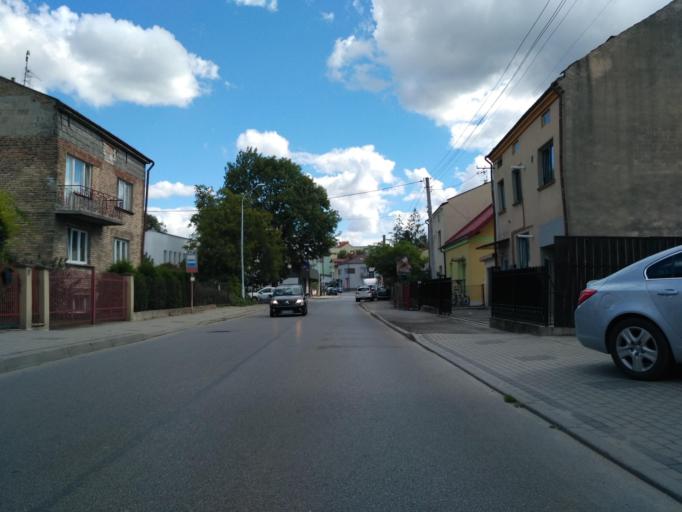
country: PL
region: Subcarpathian Voivodeship
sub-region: Powiat jasielski
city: Jaslo
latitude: 49.7493
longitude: 21.4698
